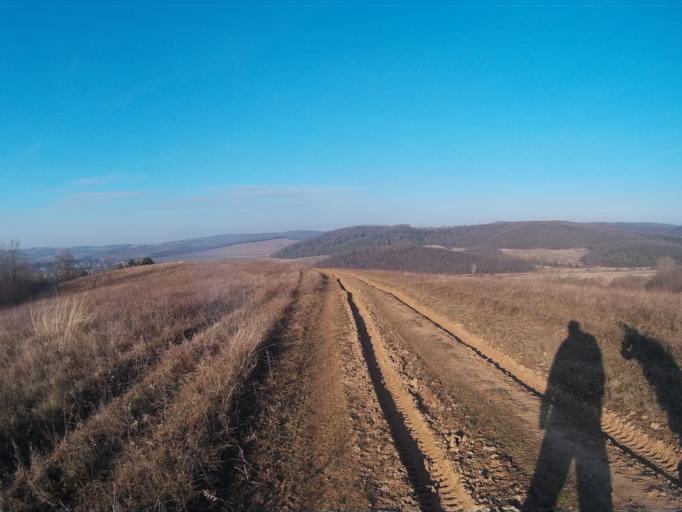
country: HU
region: Nograd
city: Bercel
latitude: 47.9708
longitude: 19.4390
